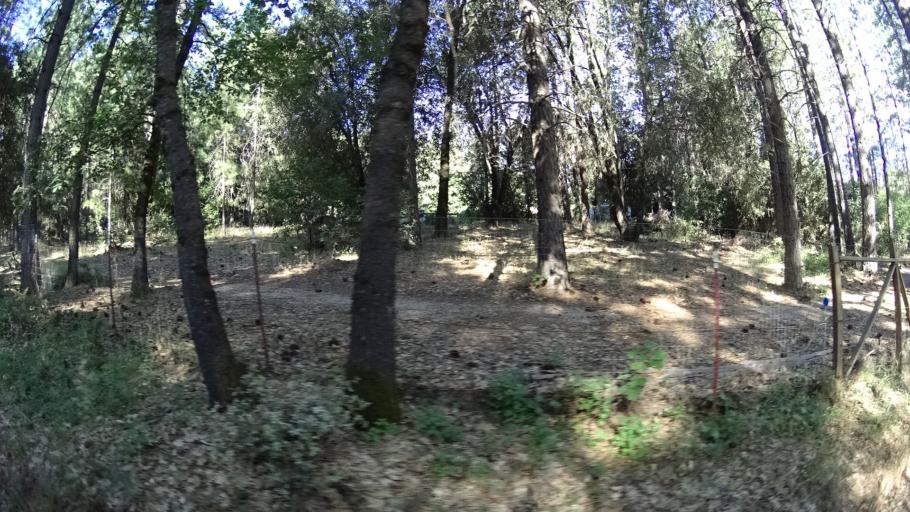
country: US
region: California
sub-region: Amador County
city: Pioneer
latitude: 38.3848
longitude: -120.5560
